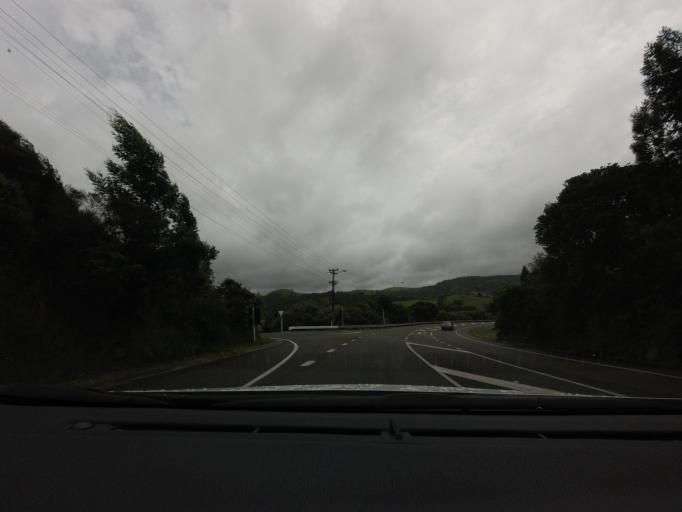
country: NZ
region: Auckland
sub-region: Auckland
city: Rothesay Bay
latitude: -36.5691
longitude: 174.6915
